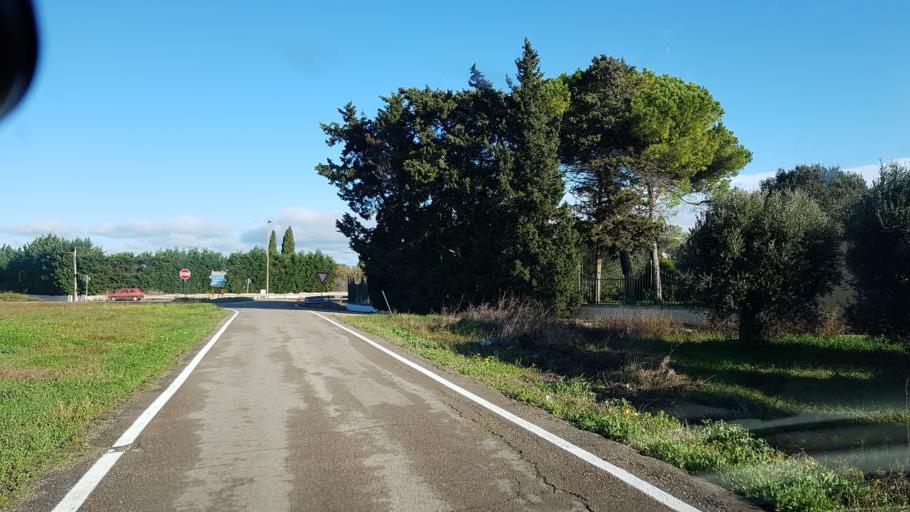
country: IT
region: Apulia
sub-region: Provincia di Brindisi
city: Tuturano
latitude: 40.5542
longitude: 17.9966
